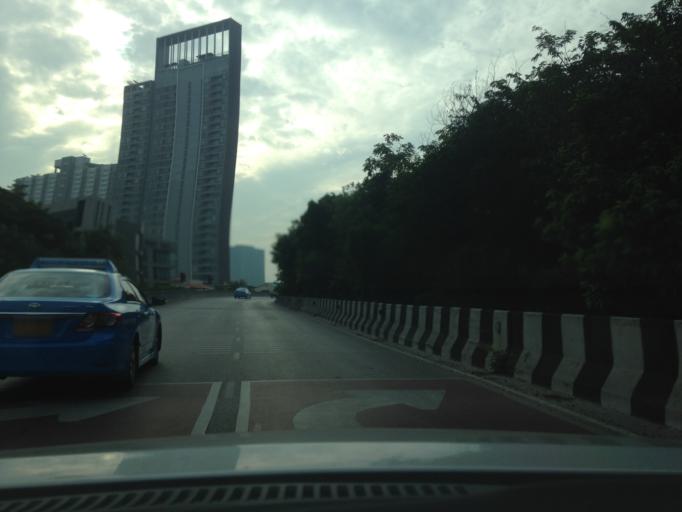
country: TH
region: Bangkok
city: Chatuchak
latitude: 13.8322
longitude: 100.5581
